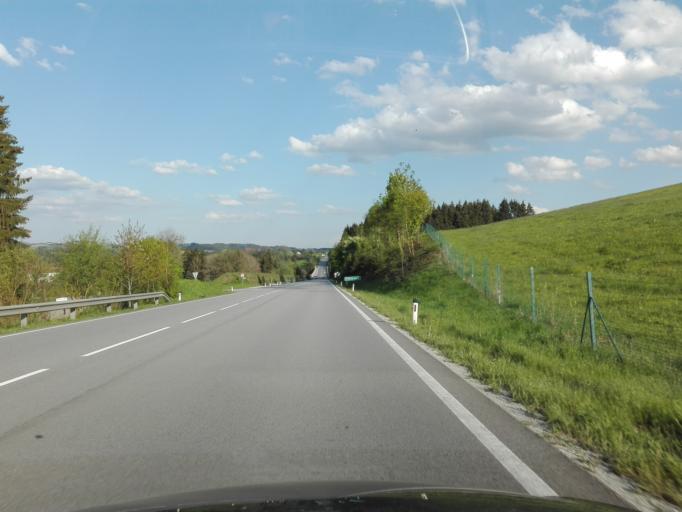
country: AT
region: Upper Austria
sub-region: Politischer Bezirk Rohrbach
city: Kleinzell im Muehlkreis
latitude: 48.4801
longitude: 13.9888
